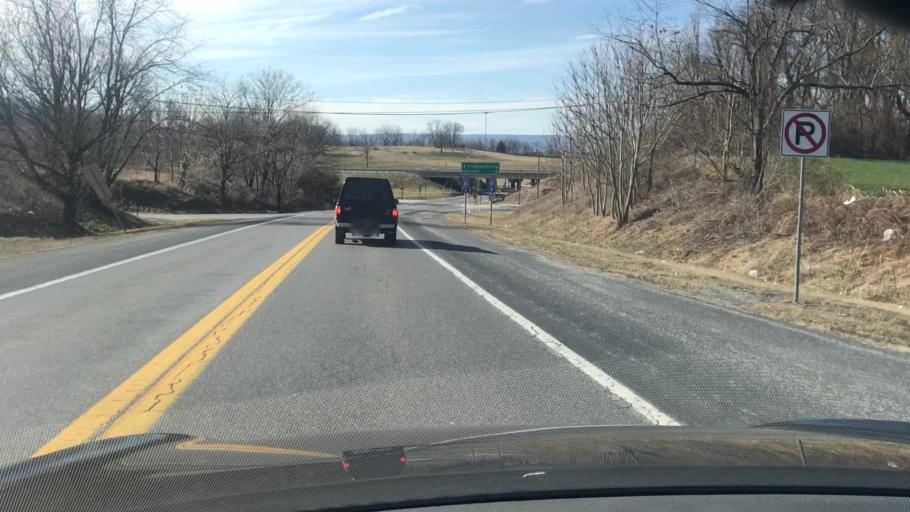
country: US
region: Pennsylvania
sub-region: Cumberland County
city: Newville
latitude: 40.1274
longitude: -77.3479
